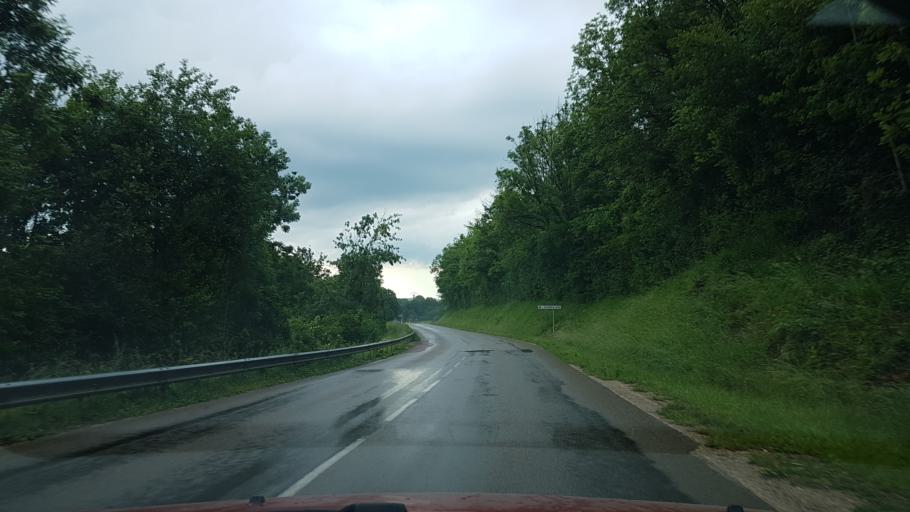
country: FR
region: Franche-Comte
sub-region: Departement du Jura
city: Clairvaux-les-Lacs
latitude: 46.5484
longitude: 5.7465
